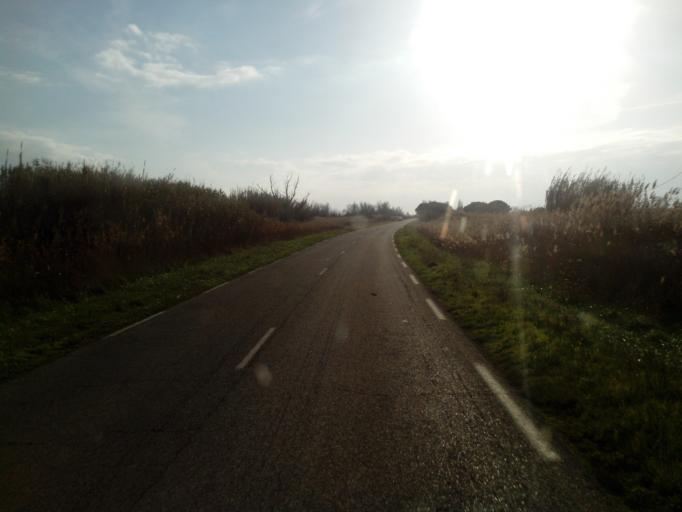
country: FR
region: Provence-Alpes-Cote d'Azur
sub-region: Departement des Bouches-du-Rhone
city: Port-Saint-Louis-du-Rhone
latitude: 43.4454
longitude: 4.7260
